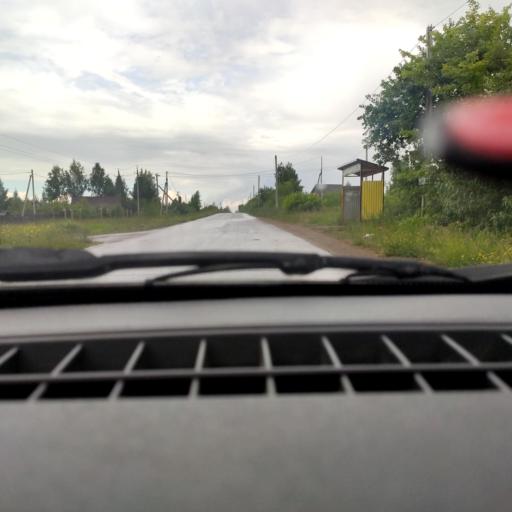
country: RU
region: Bashkortostan
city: Kabakovo
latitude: 54.5684
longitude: 56.2717
